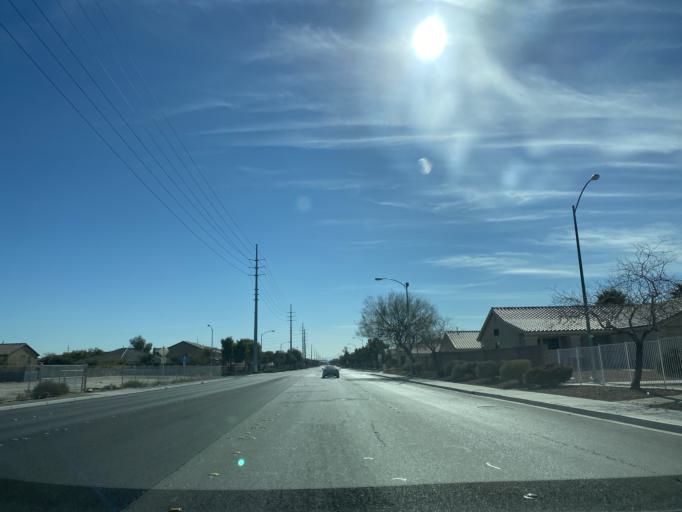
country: US
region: Nevada
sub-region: Clark County
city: North Las Vegas
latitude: 36.2736
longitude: -115.1441
